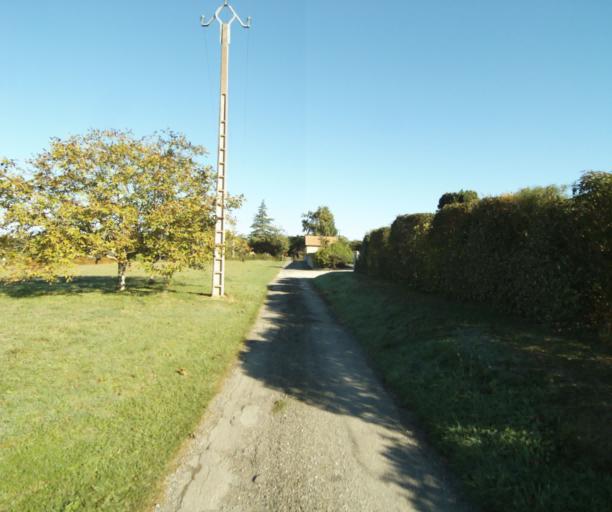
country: FR
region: Midi-Pyrenees
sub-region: Departement du Gers
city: Gondrin
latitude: 43.8383
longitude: 0.2544
